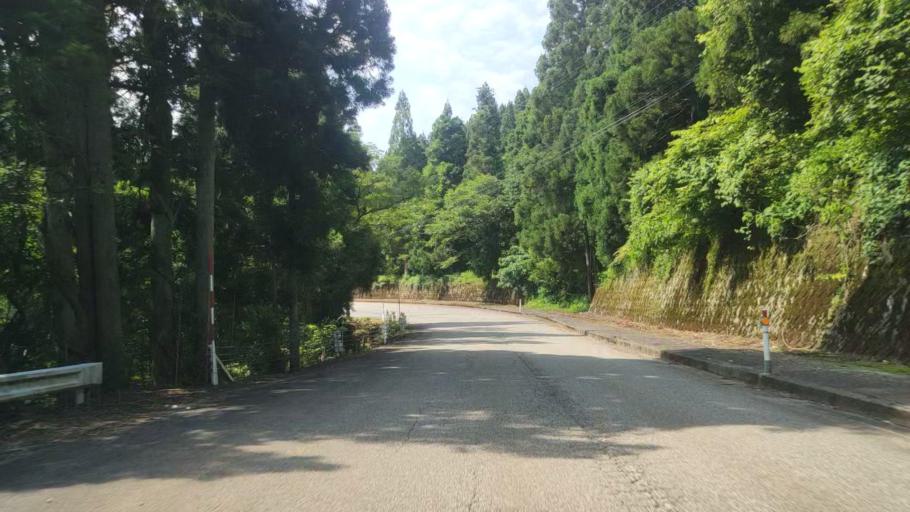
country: JP
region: Ishikawa
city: Komatsu
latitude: 36.3017
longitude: 136.5281
